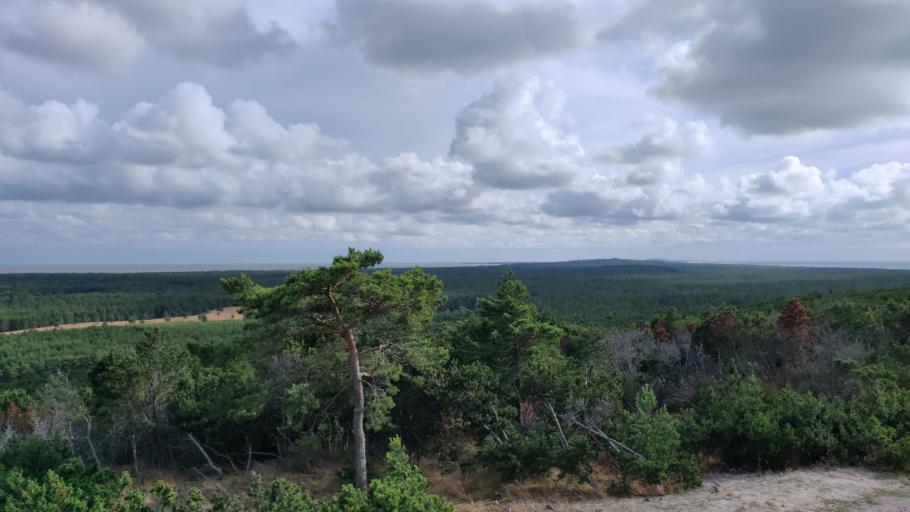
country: LT
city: Neringa
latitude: 55.3546
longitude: 21.0384
